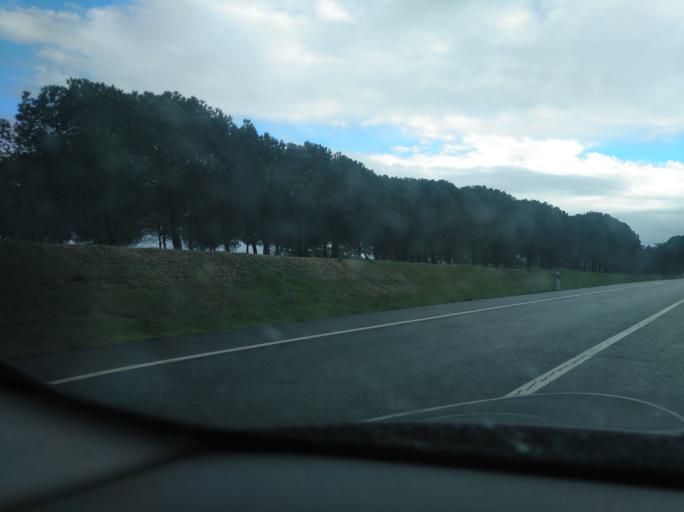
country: PT
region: Beja
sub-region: Aljustrel
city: Aljustrel
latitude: 37.9540
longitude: -8.3811
